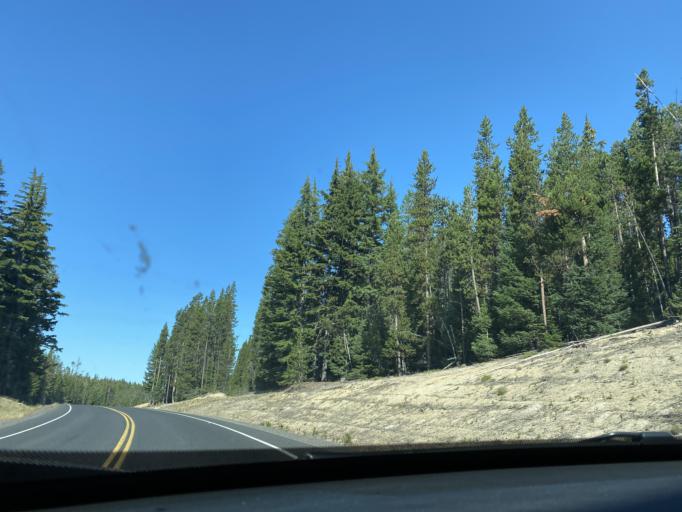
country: US
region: Oregon
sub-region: Deschutes County
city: Three Rivers
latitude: 43.7044
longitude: -121.2603
